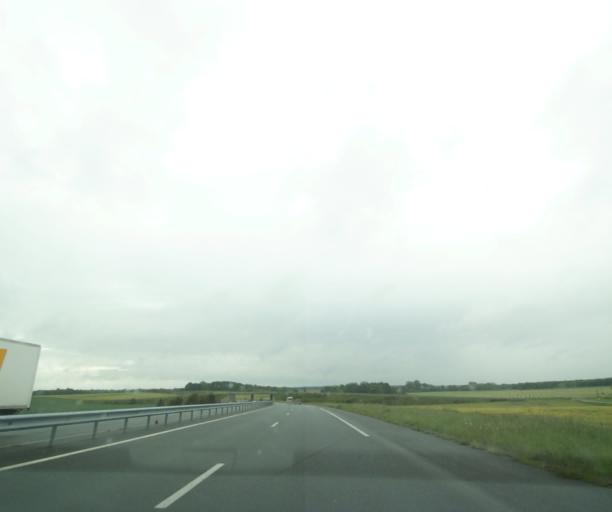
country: FR
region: Poitou-Charentes
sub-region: Departement de la Charente-Maritime
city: Nieul-les-Saintes
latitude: 45.6977
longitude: -0.7435
